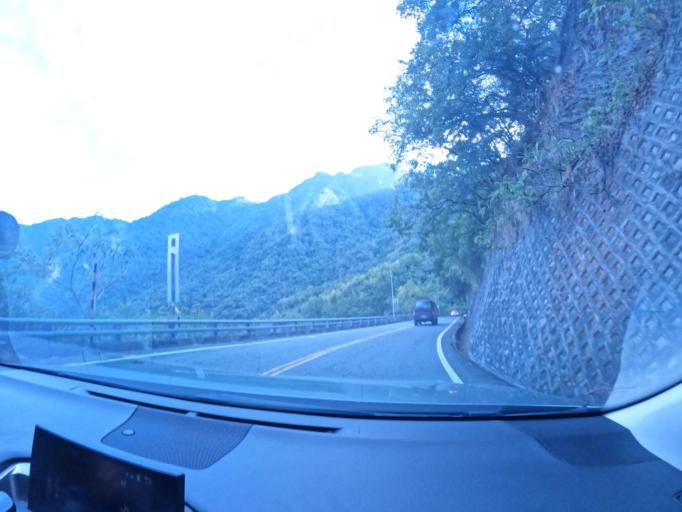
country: TW
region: Taiwan
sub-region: Taitung
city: Taitung
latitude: 23.1477
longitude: 121.0790
